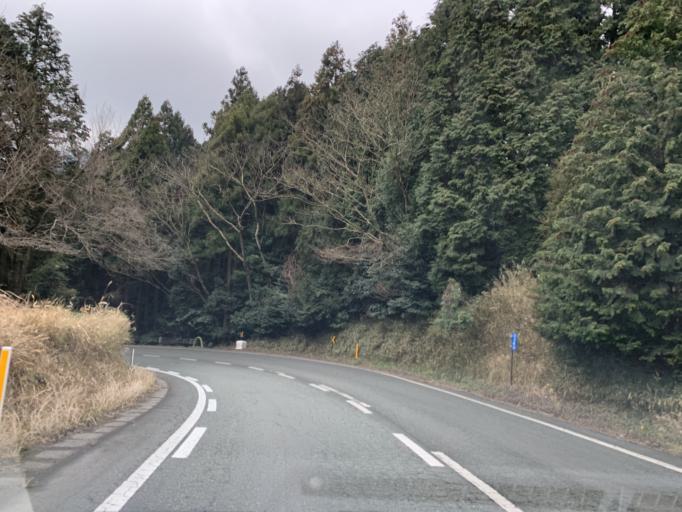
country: JP
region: Kumamoto
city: Aso
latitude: 32.9155
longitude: 130.9740
